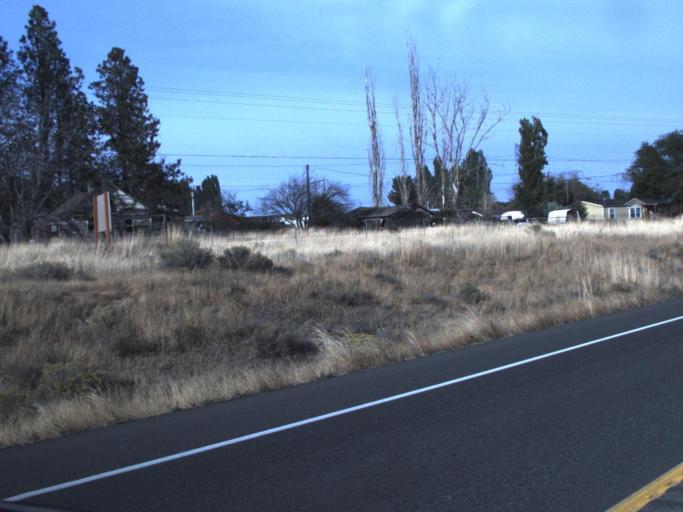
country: US
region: Oregon
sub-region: Morrow County
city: Irrigon
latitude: 45.9380
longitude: -119.6001
